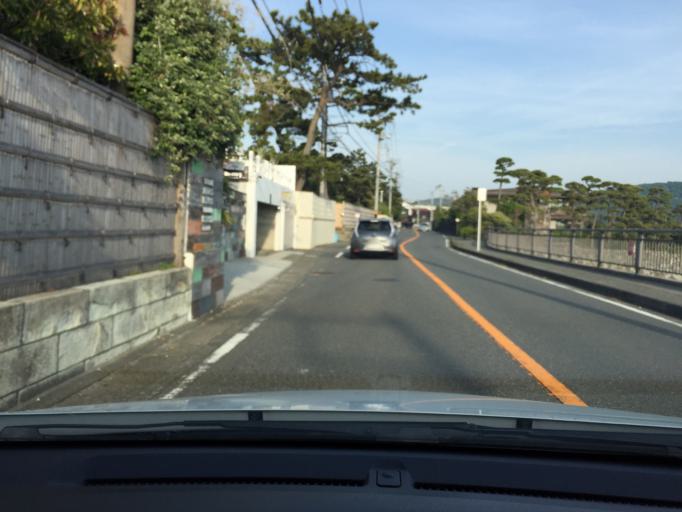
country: JP
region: Kanagawa
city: Hayama
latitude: 35.2664
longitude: 139.5720
